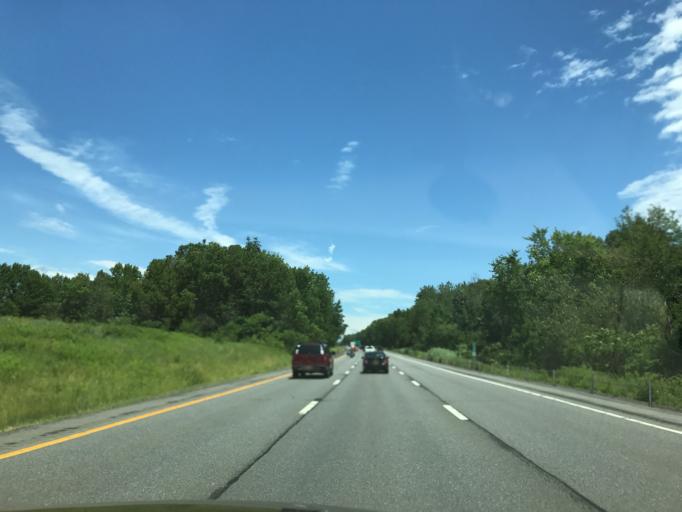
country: US
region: New York
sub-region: Warren County
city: West Glens Falls
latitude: 43.2048
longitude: -73.6953
